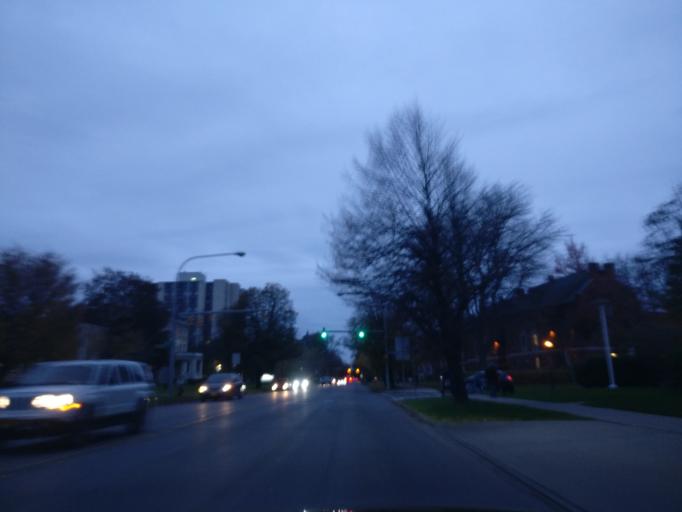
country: US
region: New York
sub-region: Erie County
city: Buffalo
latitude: 42.9135
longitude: -78.8698
